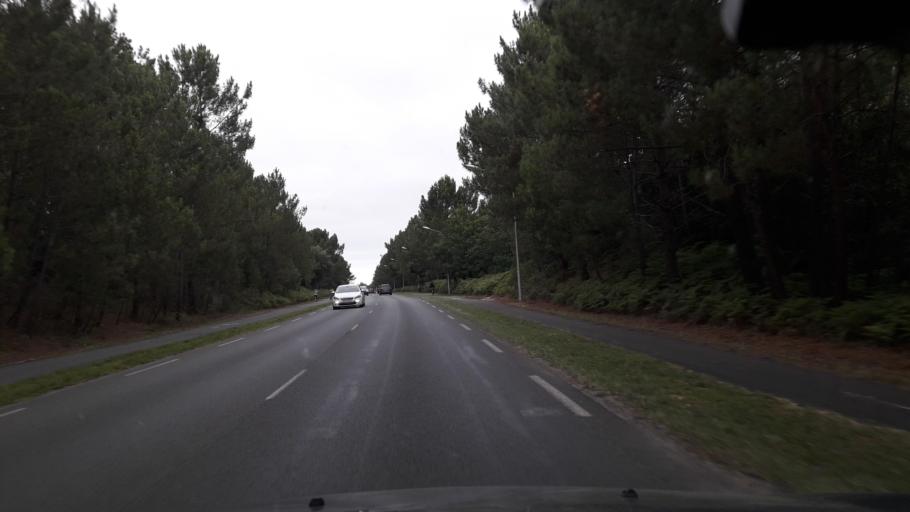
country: FR
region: Poitou-Charentes
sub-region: Departement de la Charente-Maritime
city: Les Mathes
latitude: 45.7071
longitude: -1.1628
